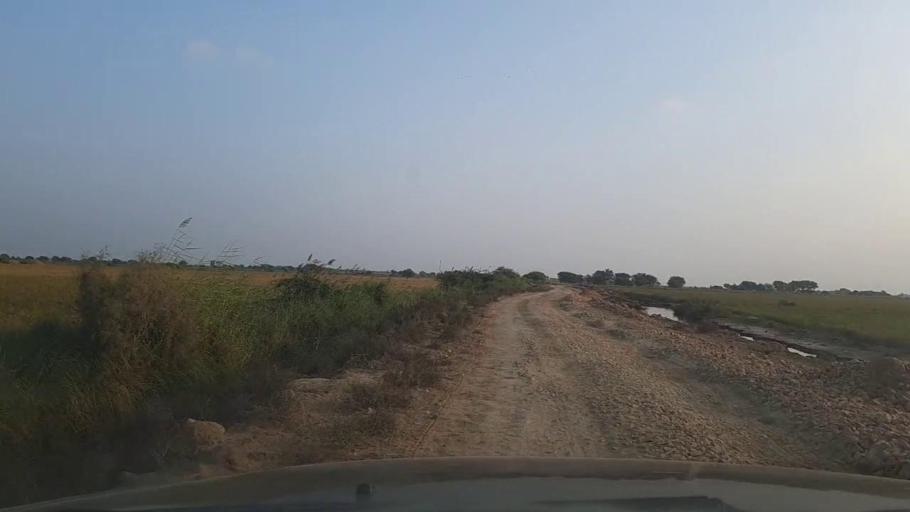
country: PK
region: Sindh
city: Jati
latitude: 24.5400
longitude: 68.3599
